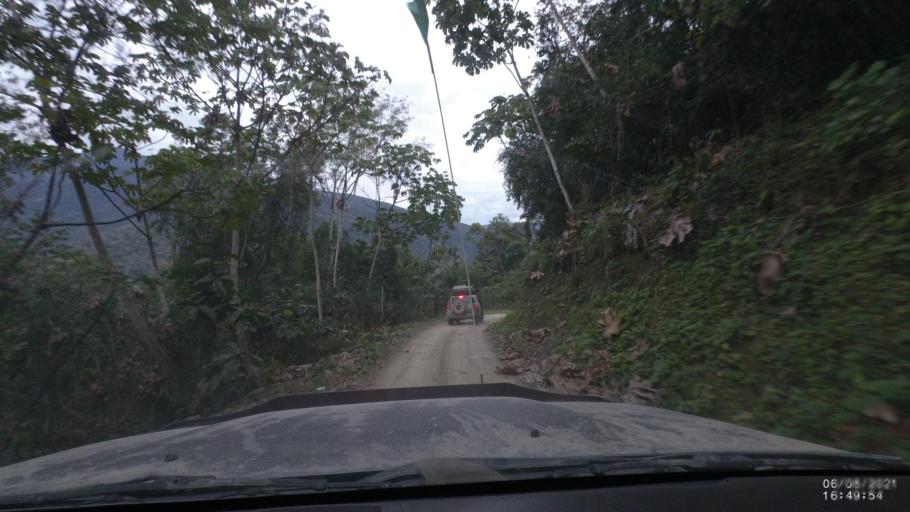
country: BO
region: La Paz
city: Quime
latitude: -16.4996
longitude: -66.7691
